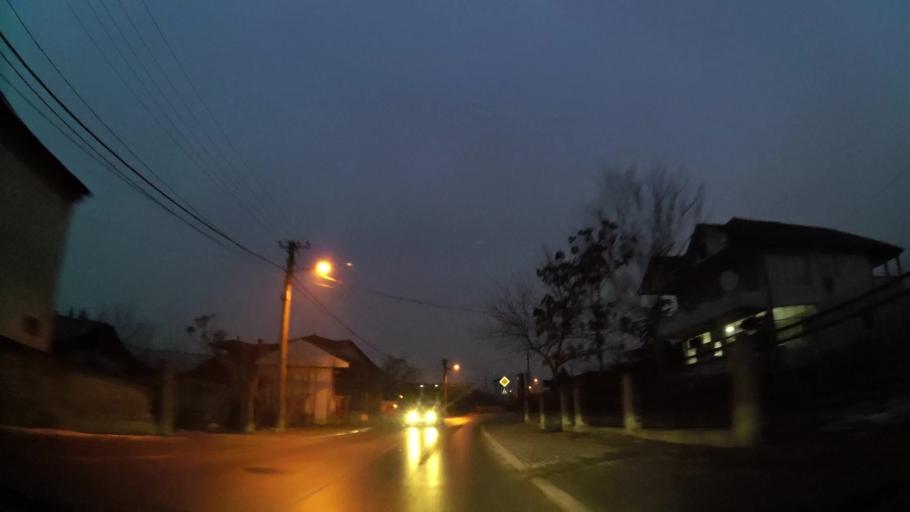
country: MK
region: Kisela Voda
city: Usje
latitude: 41.9713
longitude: 21.4816
